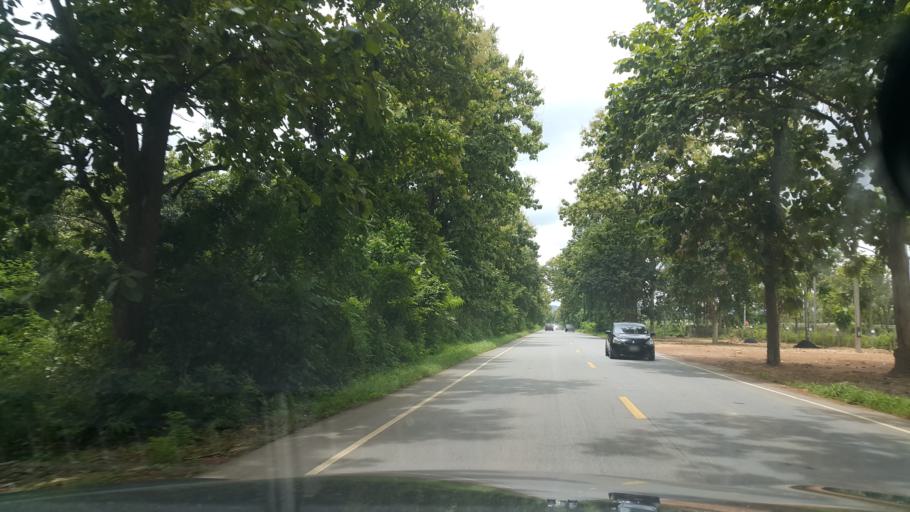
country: TH
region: Sukhothai
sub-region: Amphoe Si Satchanalai
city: Si Satchanalai
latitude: 17.5391
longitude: 99.8102
